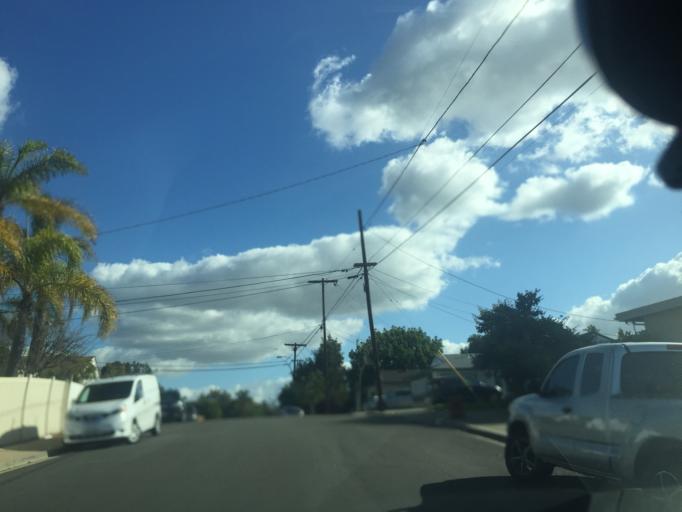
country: US
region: California
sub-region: San Diego County
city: La Mesa
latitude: 32.7840
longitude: -117.0924
